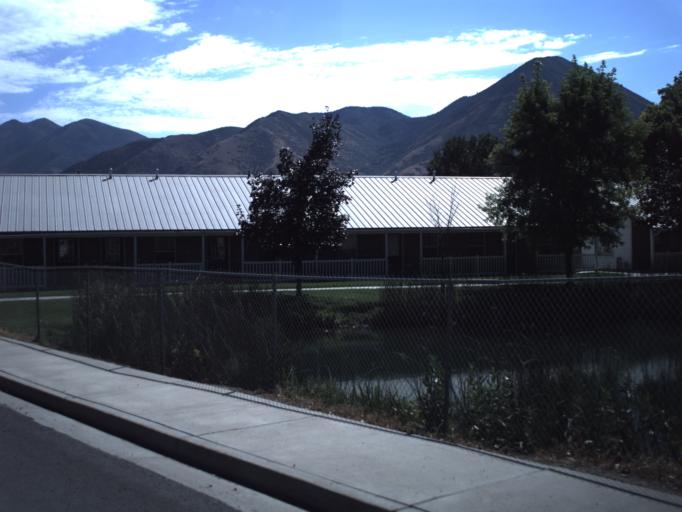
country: US
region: Utah
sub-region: Utah County
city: Salem
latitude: 40.0536
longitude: -111.6789
